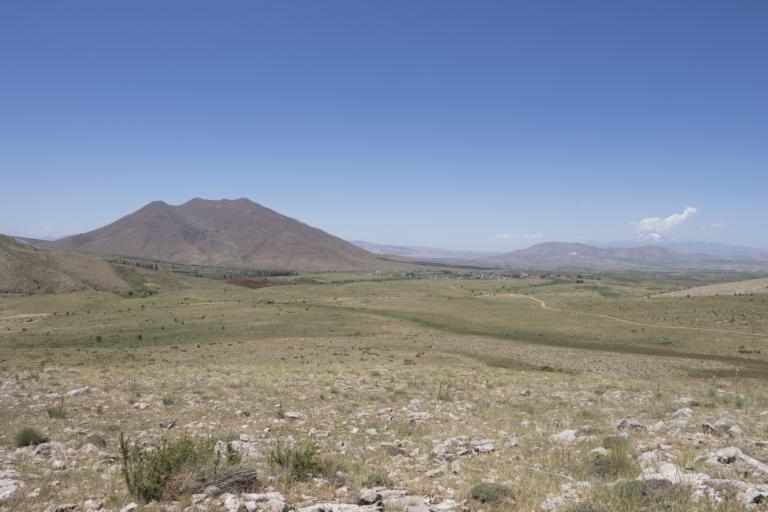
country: TR
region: Kayseri
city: Toklar
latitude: 38.4068
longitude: 36.1154
